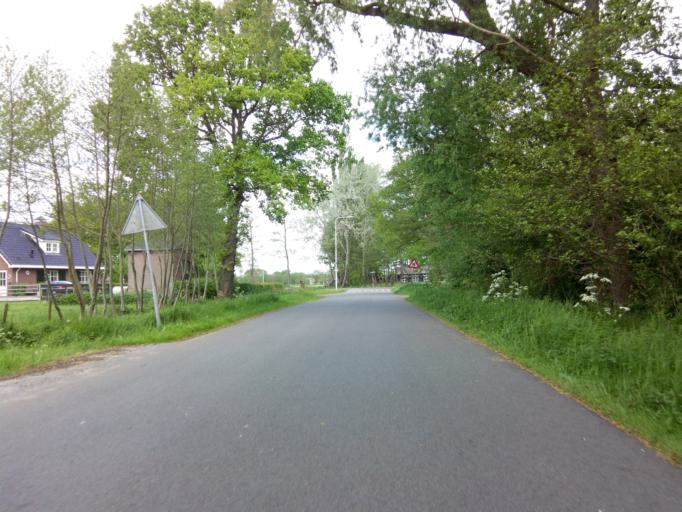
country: NL
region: Gelderland
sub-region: Gemeente Ede
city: Lunteren
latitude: 52.0698
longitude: 5.6239
